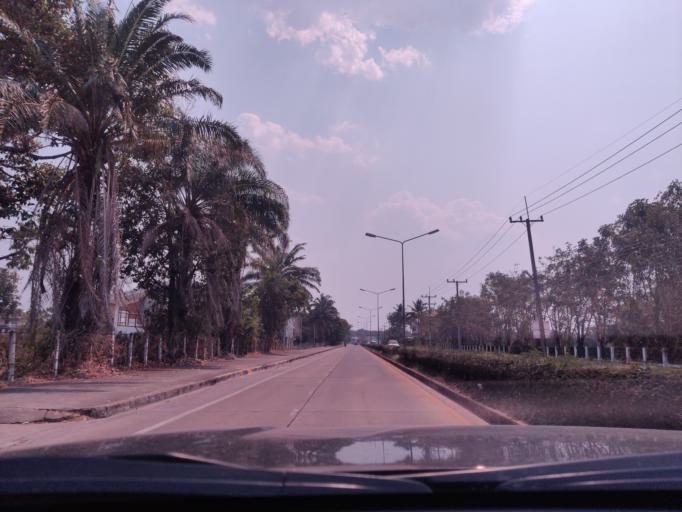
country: TH
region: Sisaket
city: Si Sa Ket
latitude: 15.1038
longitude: 104.3152
